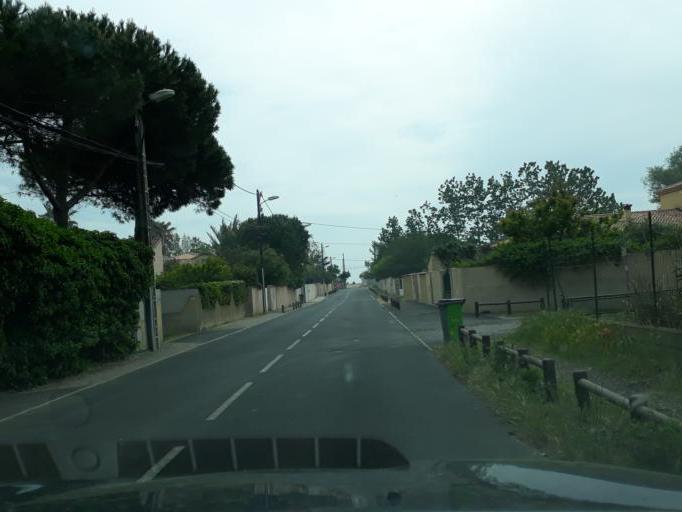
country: FR
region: Languedoc-Roussillon
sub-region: Departement de l'Herault
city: Agde
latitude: 43.2793
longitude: 3.4675
